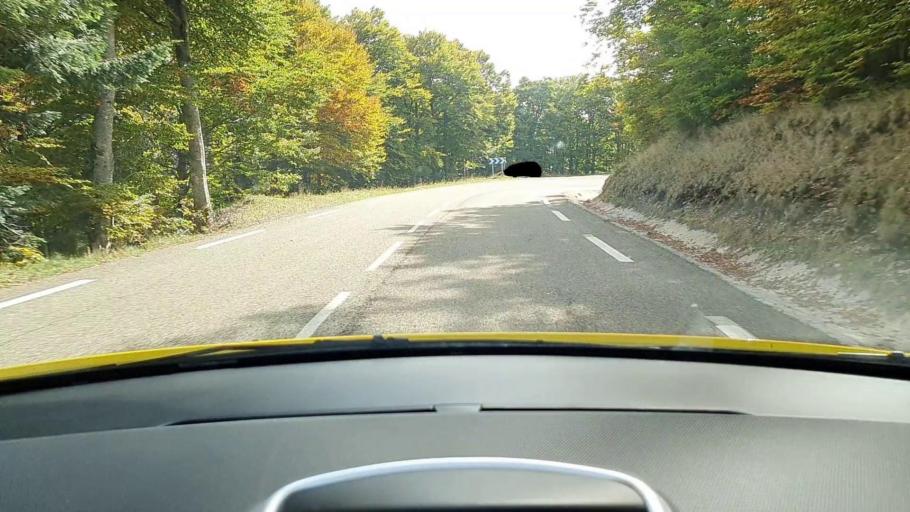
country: FR
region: Languedoc-Roussillon
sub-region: Departement du Gard
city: Valleraugue
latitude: 44.1063
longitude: 3.5476
